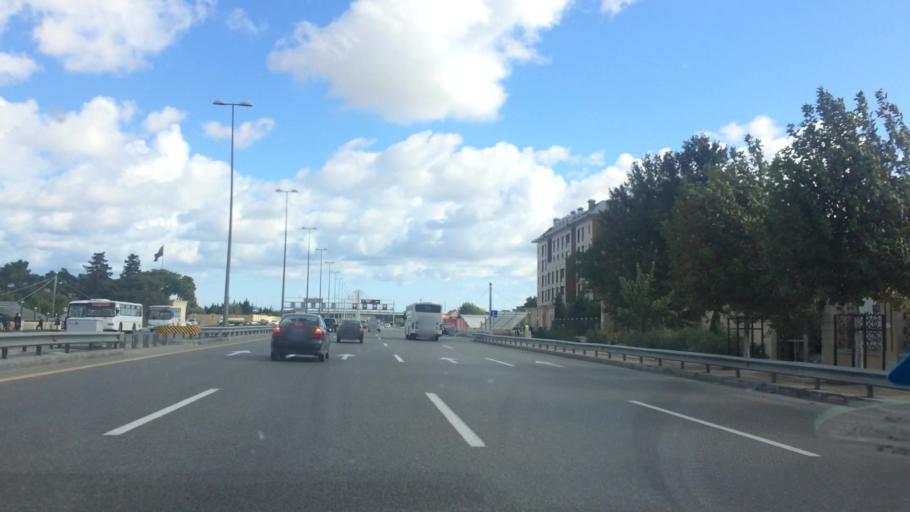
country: AZ
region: Baki
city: Biny Selo
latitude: 40.4551
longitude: 50.0678
